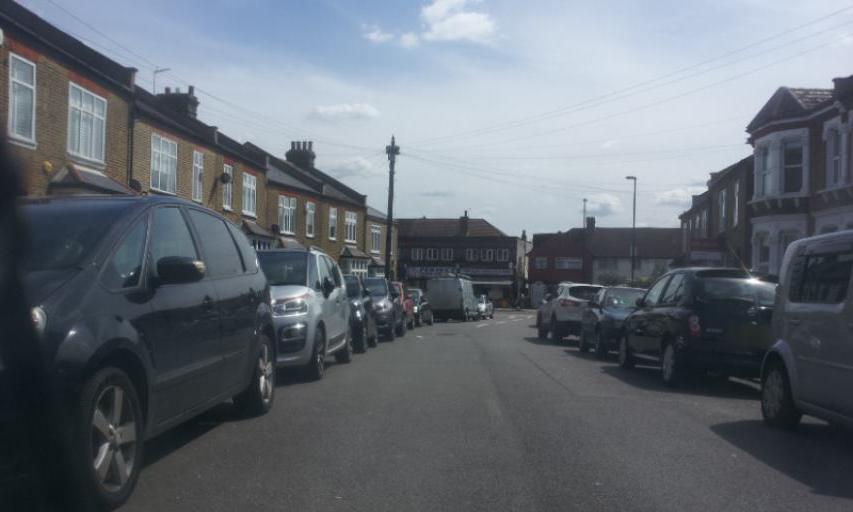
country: GB
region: England
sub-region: Greater London
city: Catford
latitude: 51.4532
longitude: -0.0395
